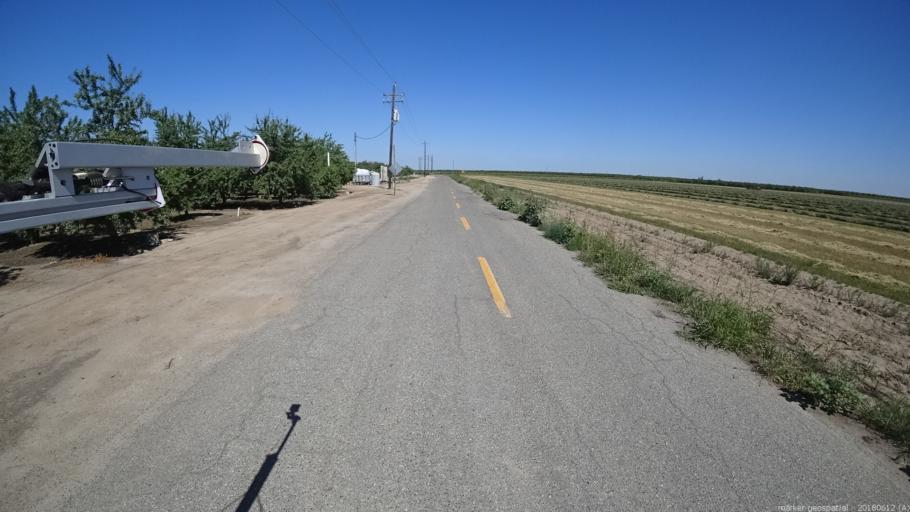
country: US
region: California
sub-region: Madera County
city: Chowchilla
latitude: 37.0314
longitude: -120.3442
